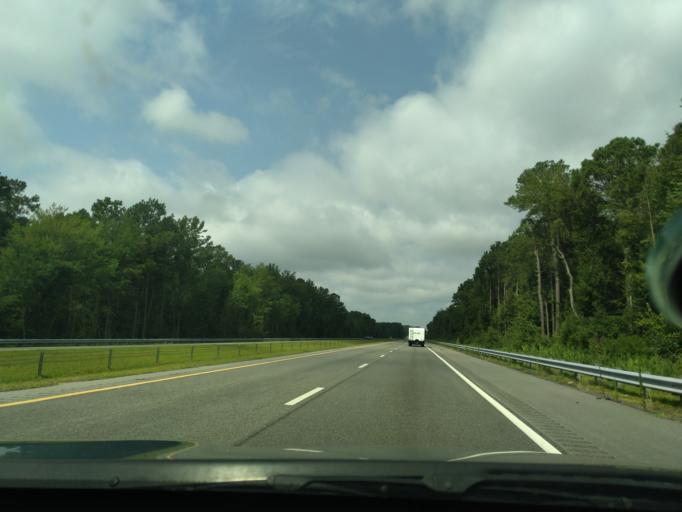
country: US
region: North Carolina
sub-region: Pitt County
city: Bethel
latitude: 35.8324
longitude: -77.3277
